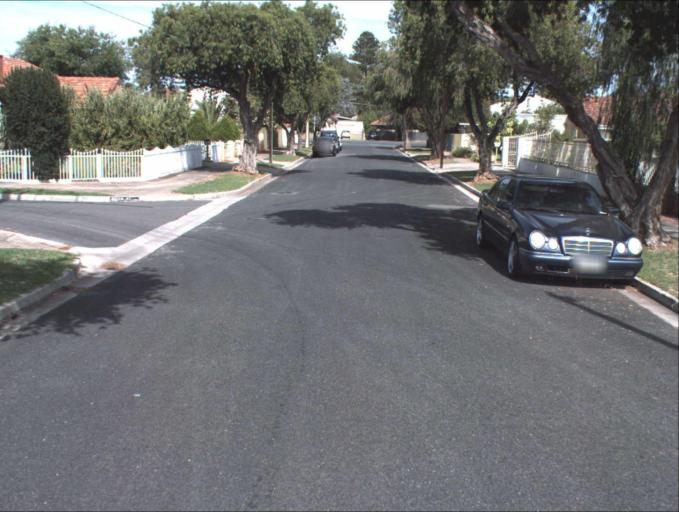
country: AU
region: South Australia
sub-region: Port Adelaide Enfield
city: Klemzig
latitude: -34.8790
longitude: 138.6209
